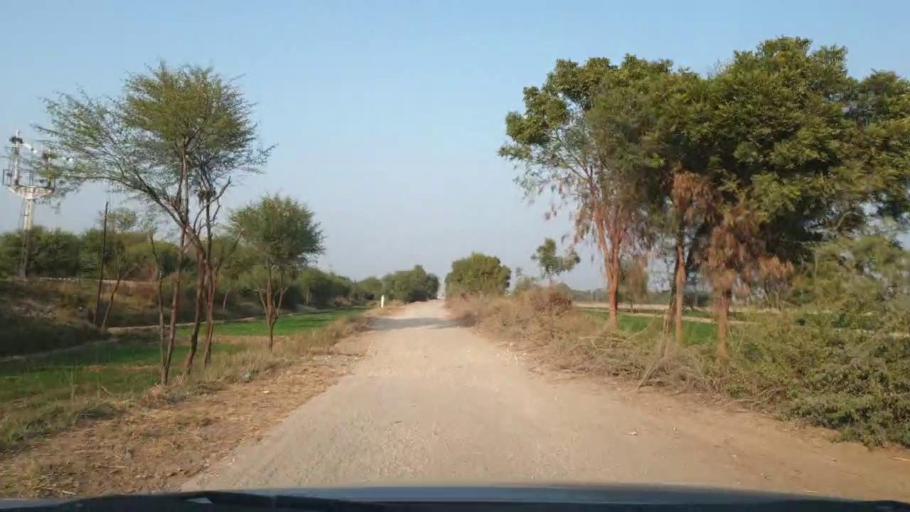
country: PK
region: Sindh
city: Tando Adam
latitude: 25.6943
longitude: 68.6353
